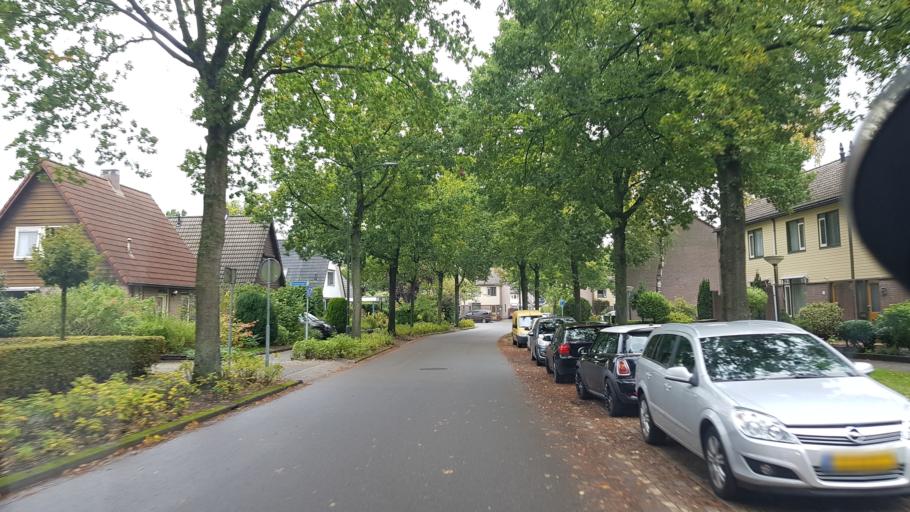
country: NL
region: Gelderland
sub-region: Gemeente Apeldoorn
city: Beekbergen
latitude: 52.1830
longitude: 5.9450
